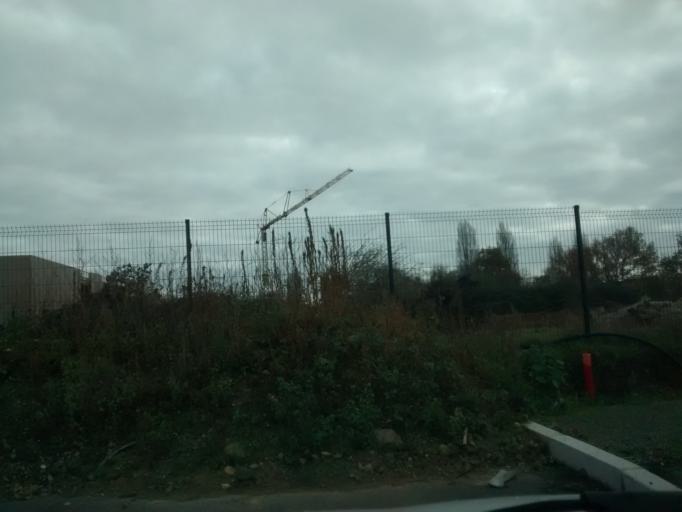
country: FR
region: Brittany
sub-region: Departement d'Ille-et-Vilaine
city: Vezin-le-Coquet
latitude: 48.1097
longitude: -1.7262
